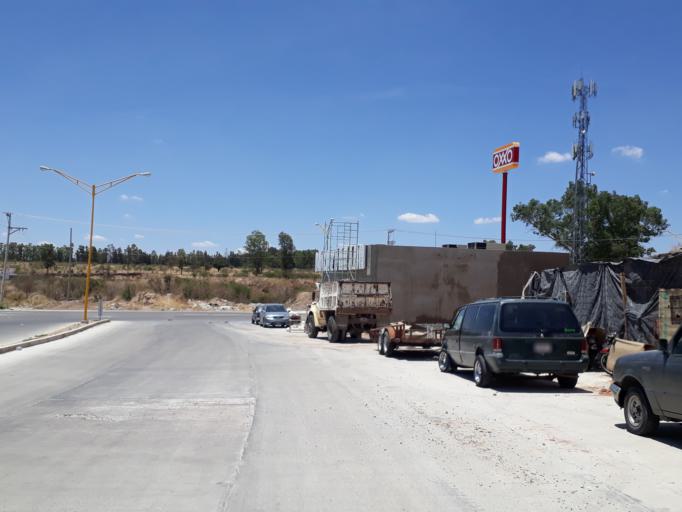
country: MX
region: Aguascalientes
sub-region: Aguascalientes
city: San Sebastian [Fraccionamiento]
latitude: 21.8086
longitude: -102.2993
